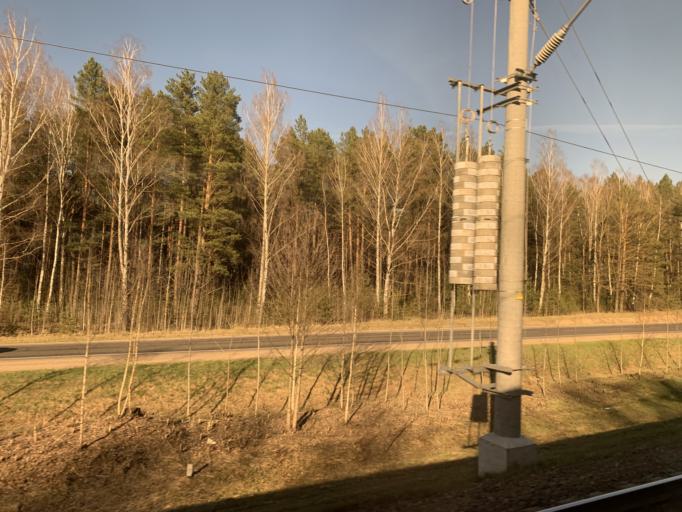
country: BY
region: Grodnenskaya
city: Smarhon'
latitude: 54.4410
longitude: 26.5029
